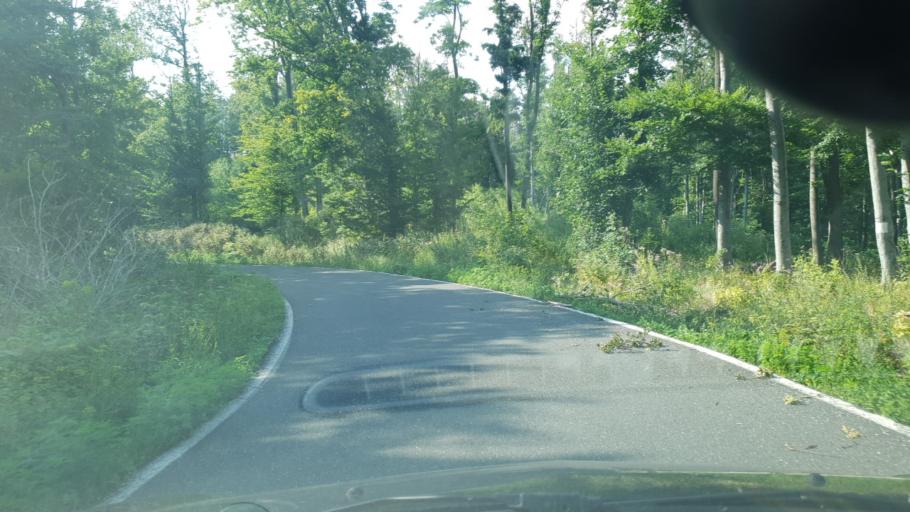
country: HR
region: Grad Zagreb
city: Kasina
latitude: 45.8872
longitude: 15.9642
